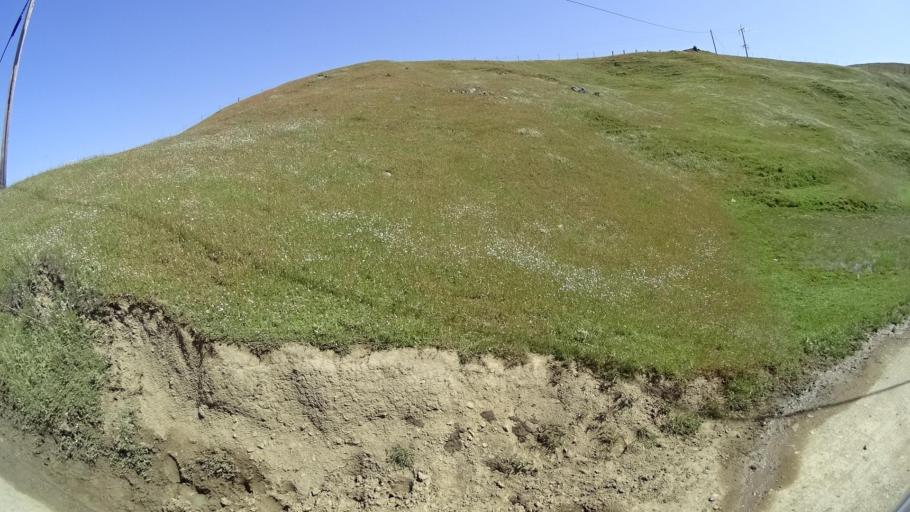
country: US
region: California
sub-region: Humboldt County
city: Redway
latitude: 40.0255
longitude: -123.6319
